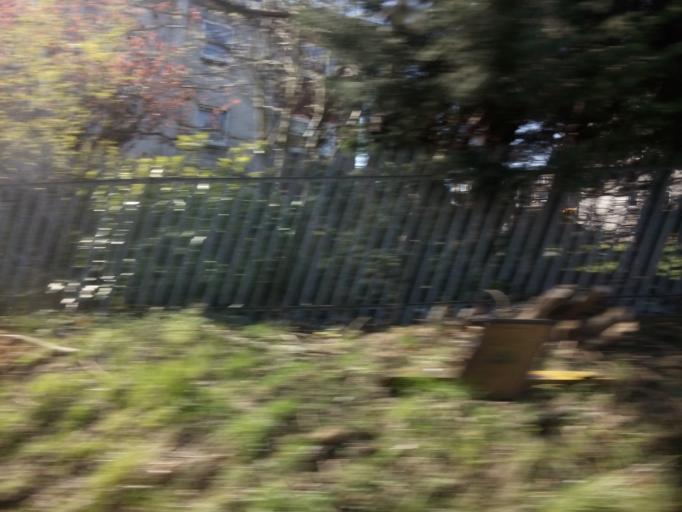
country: GB
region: Scotland
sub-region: Edinburgh
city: Colinton
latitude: 55.9335
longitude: -3.2858
